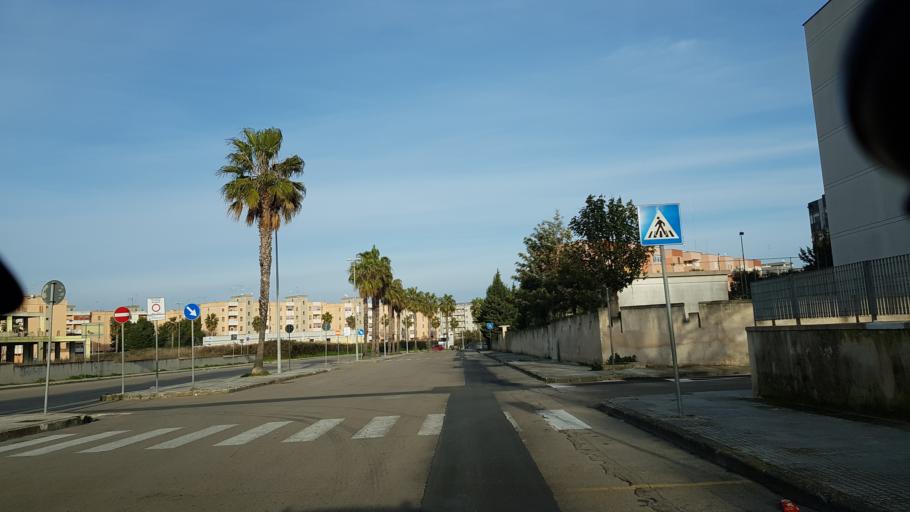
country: IT
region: Apulia
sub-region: Provincia di Brindisi
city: Brindisi
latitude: 40.6175
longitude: 17.9298
